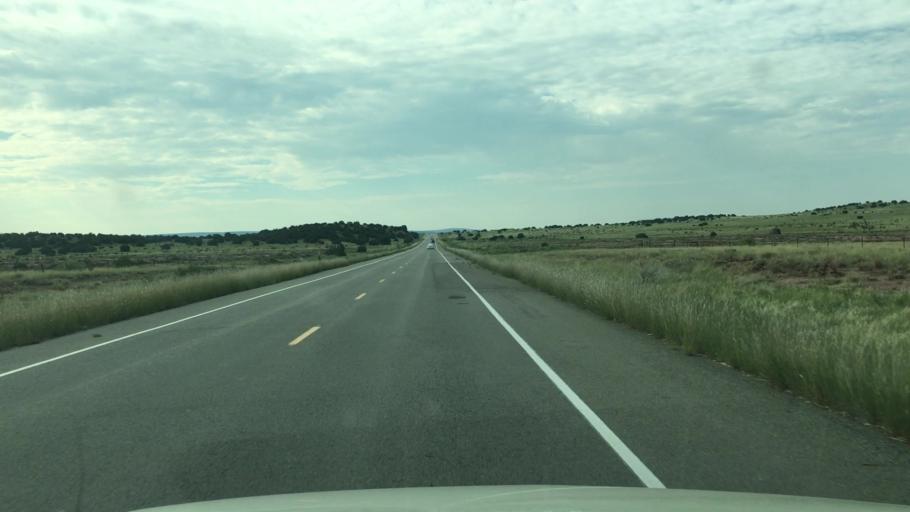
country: US
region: New Mexico
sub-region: Santa Fe County
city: Eldorado at Santa Fe
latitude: 35.4385
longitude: -105.8837
